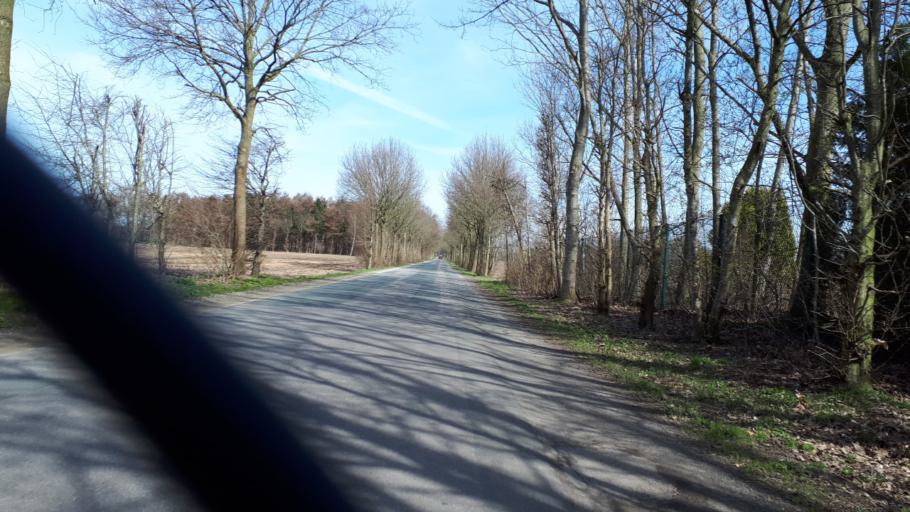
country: DE
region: Lower Saxony
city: Cloppenburg
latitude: 52.8599
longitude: 7.9941
